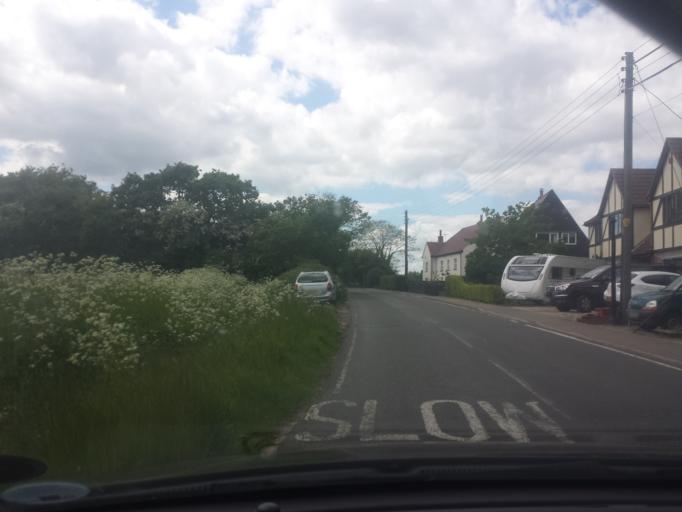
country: GB
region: England
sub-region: Essex
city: Little Clacton
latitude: 51.8815
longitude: 1.1508
